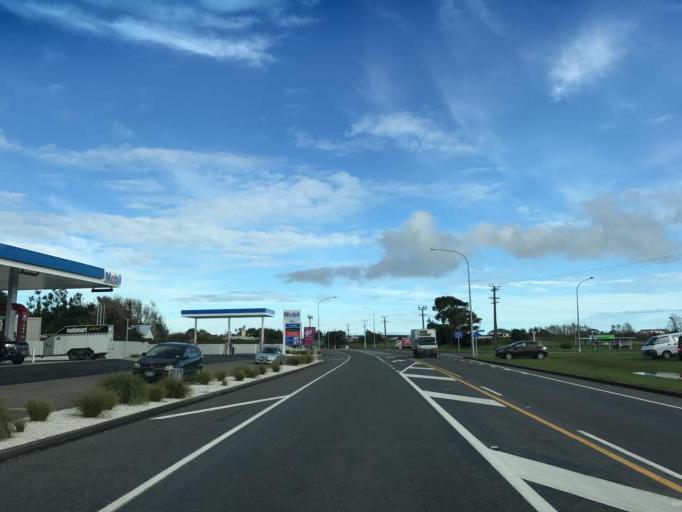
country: NZ
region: Manawatu-Wanganui
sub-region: Horowhenua District
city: Foxton
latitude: -40.4642
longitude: 175.2896
